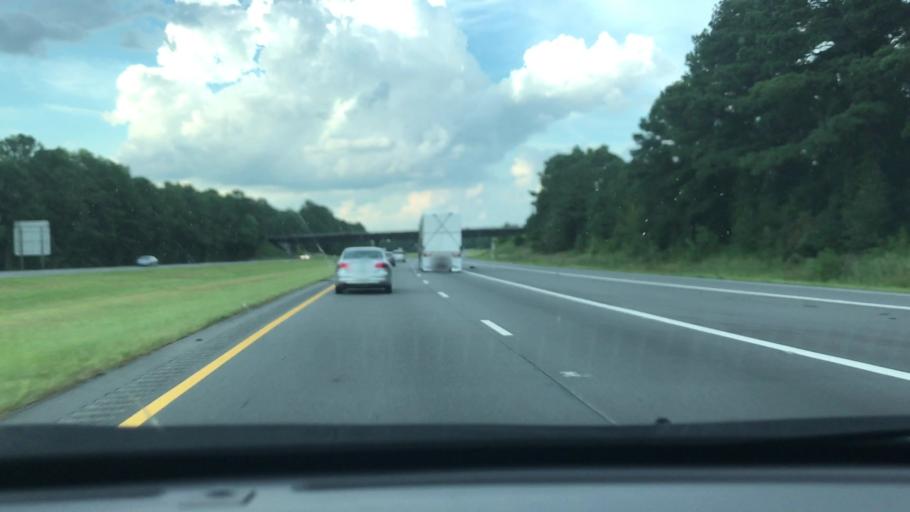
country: US
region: North Carolina
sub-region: Cumberland County
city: Vander
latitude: 35.0514
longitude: -78.8001
